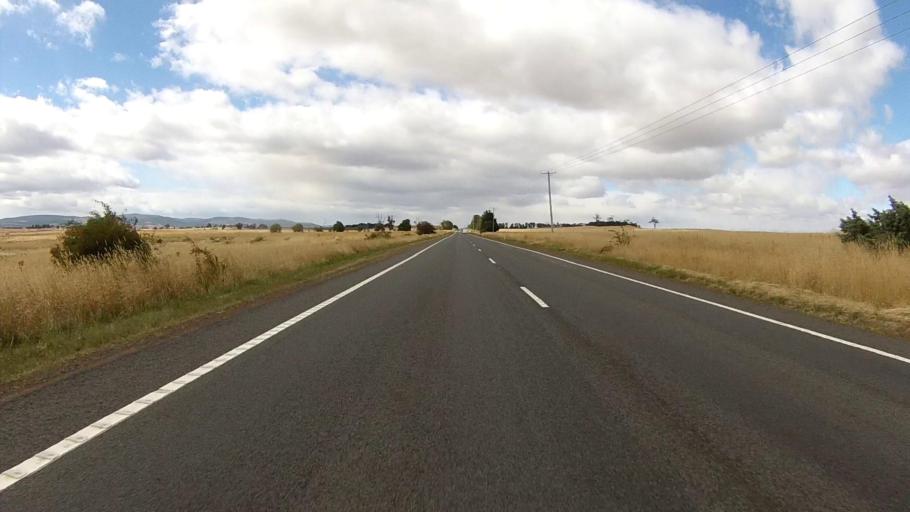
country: AU
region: Tasmania
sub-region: Northern Midlands
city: Evandale
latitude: -41.8972
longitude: 147.4741
